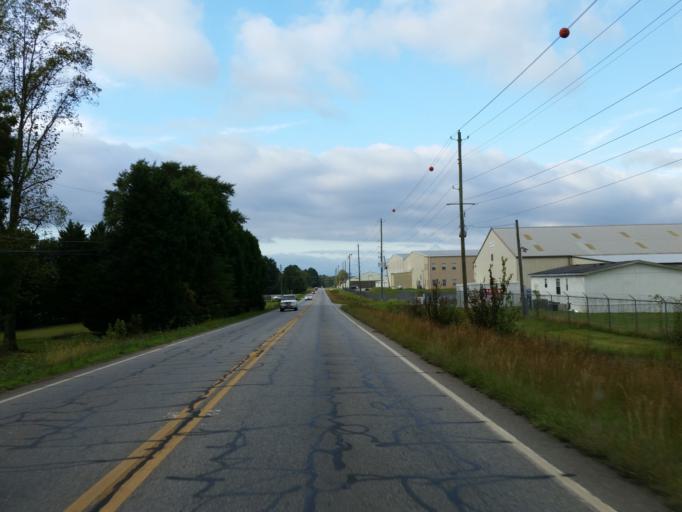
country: US
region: Georgia
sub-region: Bartow County
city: Cartersville
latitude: 34.1170
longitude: -84.8511
